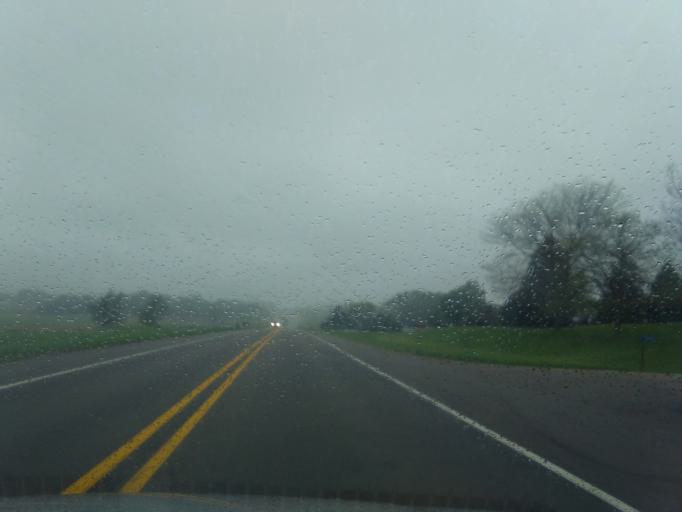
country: US
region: Nebraska
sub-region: Madison County
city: Norfolk
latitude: 42.0728
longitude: -97.3350
